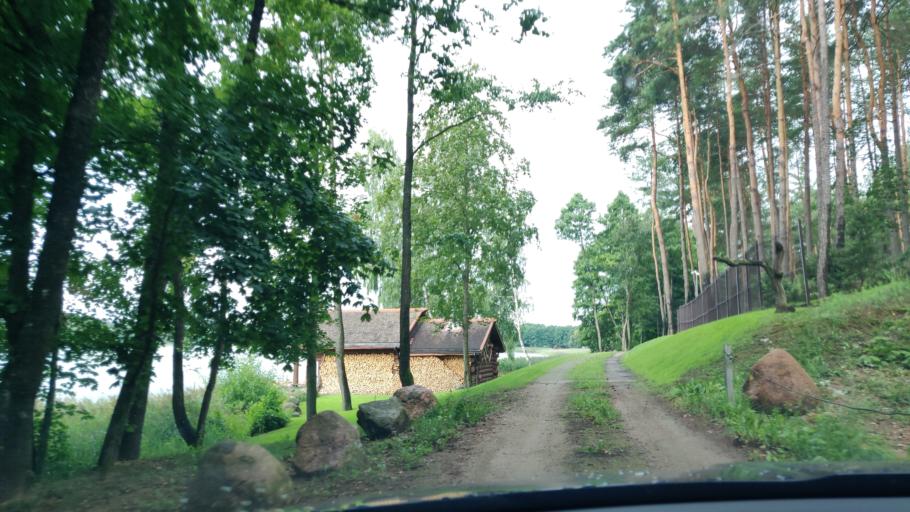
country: LT
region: Vilnius County
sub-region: Trakai
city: Rudiskes
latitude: 54.6096
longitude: 24.8288
